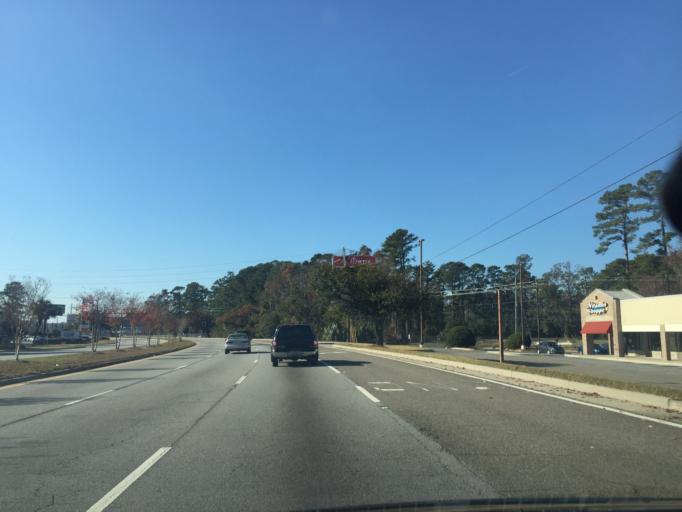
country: US
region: Georgia
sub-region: Chatham County
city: Montgomery
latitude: 32.0024
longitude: -81.1251
